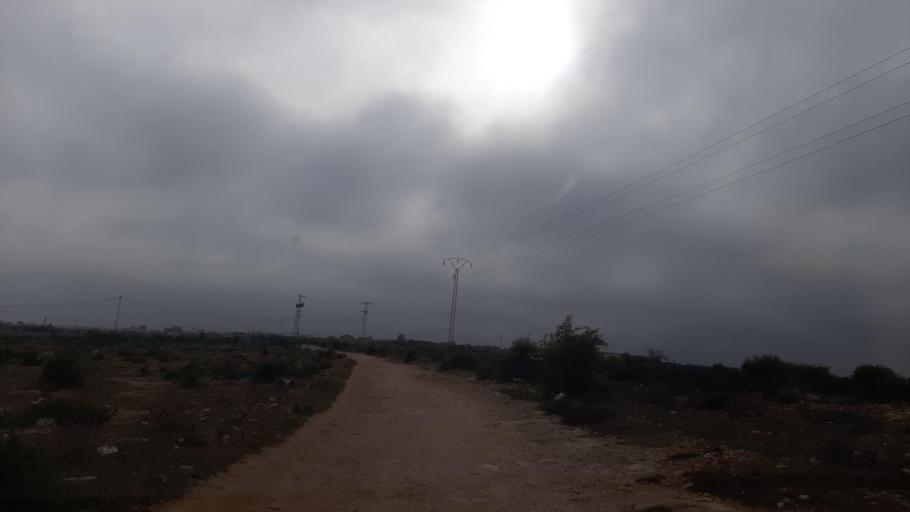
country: TN
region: Nabul
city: Menzel Heurr
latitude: 36.6909
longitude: 10.9339
